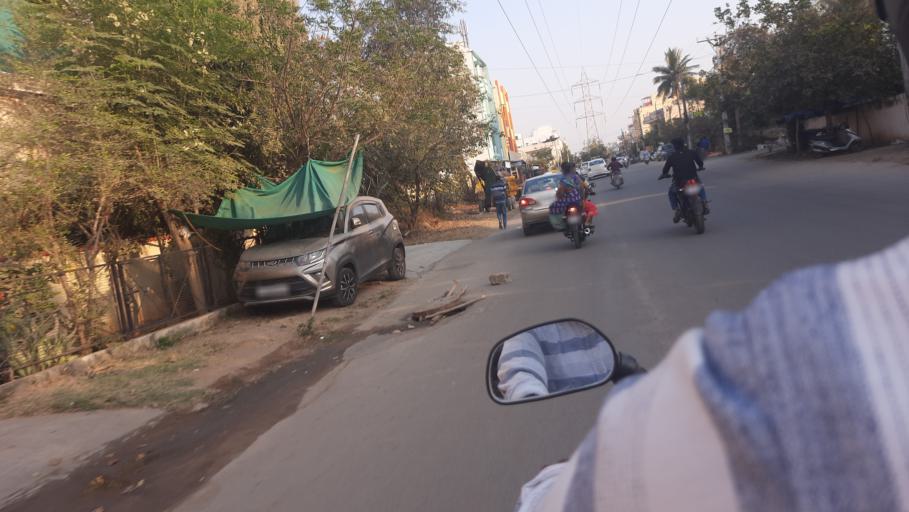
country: IN
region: Telangana
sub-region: Rangareddi
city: Secunderabad
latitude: 17.4943
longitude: 78.5455
